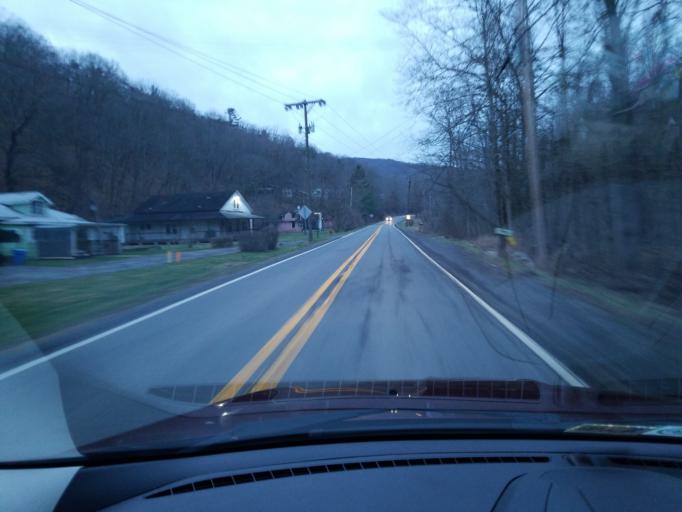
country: US
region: West Virginia
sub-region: Greenbrier County
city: Lewisburg
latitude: 37.7766
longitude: -80.3941
